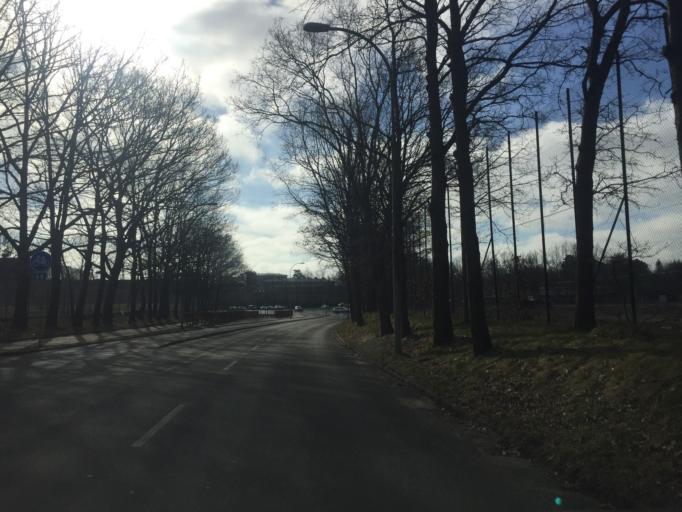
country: DK
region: Capital Region
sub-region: Lyngby-Tarbaek Kommune
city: Kongens Lyngby
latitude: 55.7587
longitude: 12.5238
